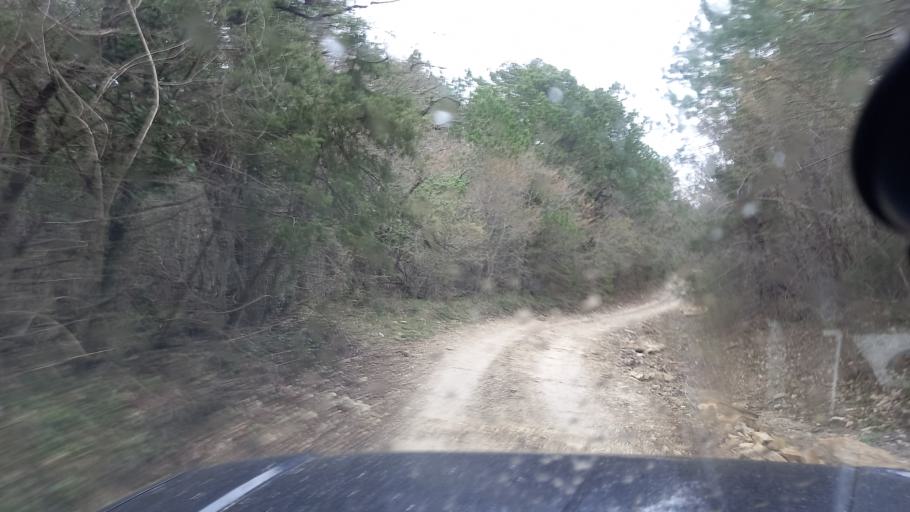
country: RU
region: Krasnodarskiy
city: Arkhipo-Osipovka
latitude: 44.3748
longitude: 38.4604
